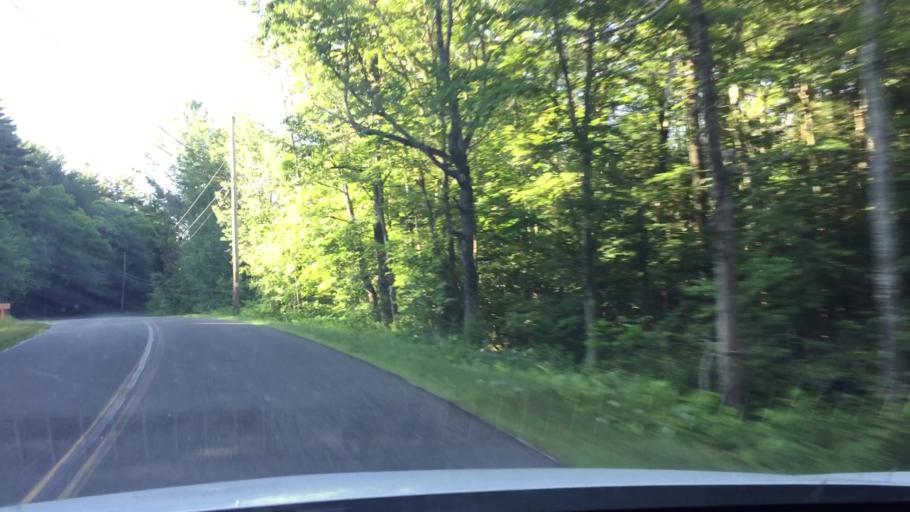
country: US
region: Massachusetts
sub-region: Berkshire County
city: Lee
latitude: 42.2792
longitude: -73.2094
